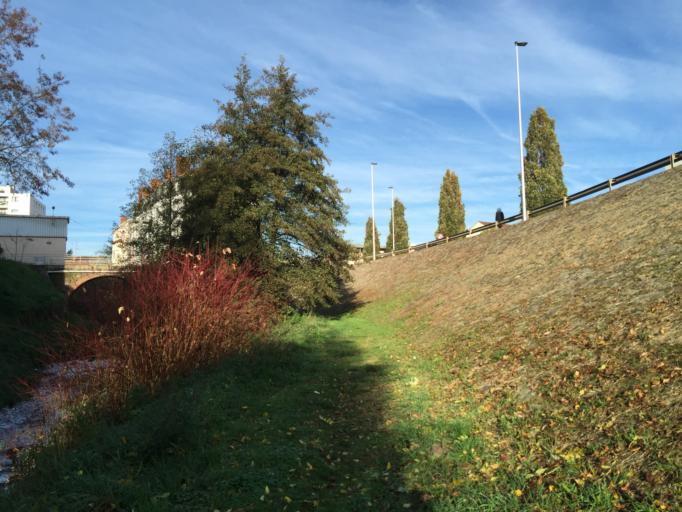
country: FR
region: Rhone-Alpes
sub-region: Departement de la Loire
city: Roanne
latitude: 46.0309
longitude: 4.0726
